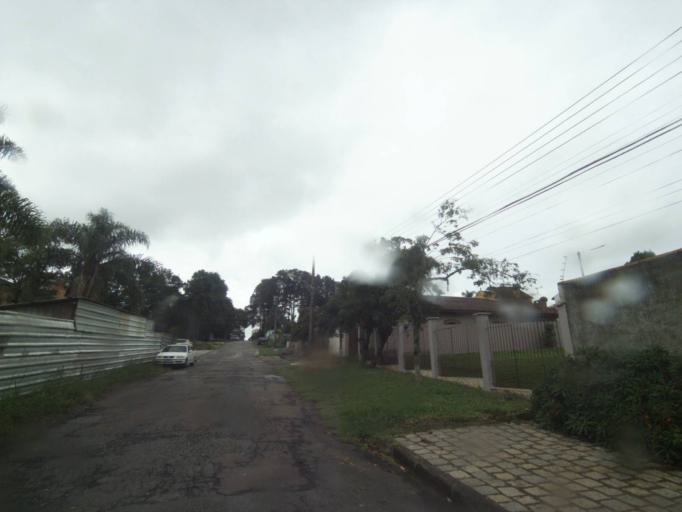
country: BR
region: Parana
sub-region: Curitiba
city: Curitiba
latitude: -25.4492
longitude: -49.3426
